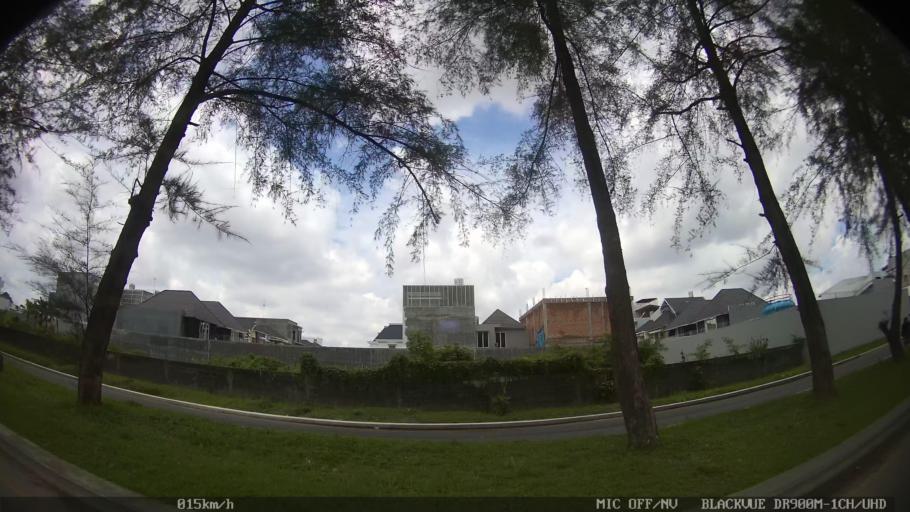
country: ID
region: North Sumatra
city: Medan
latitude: 3.6131
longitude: 98.7292
